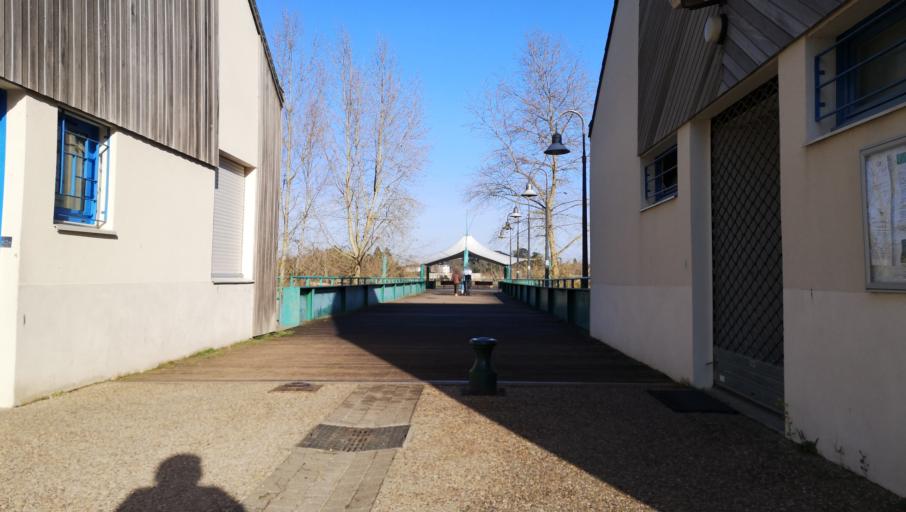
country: FR
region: Centre
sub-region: Departement du Loiret
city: Saint-Jean-le-Blanc
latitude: 47.8951
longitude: 1.9402
